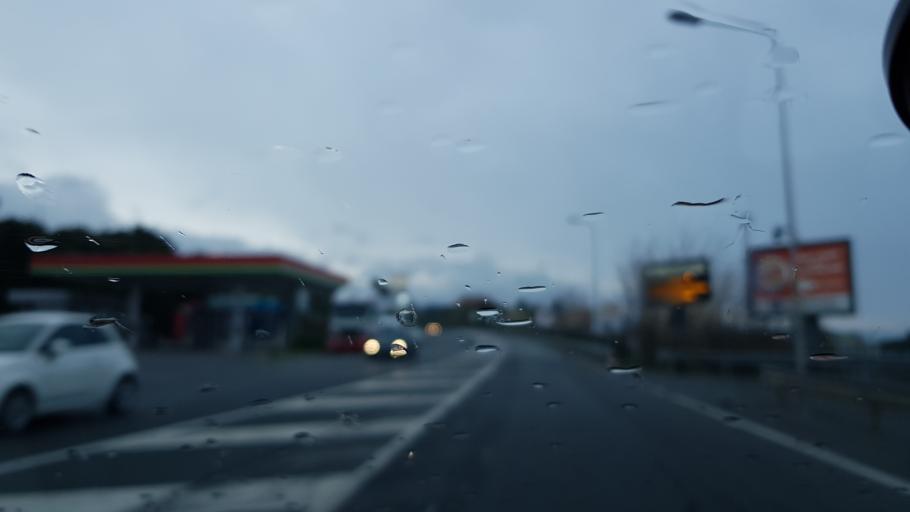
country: IT
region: Liguria
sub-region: Provincia di Savona
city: Valleggia
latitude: 44.2890
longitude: 8.4489
